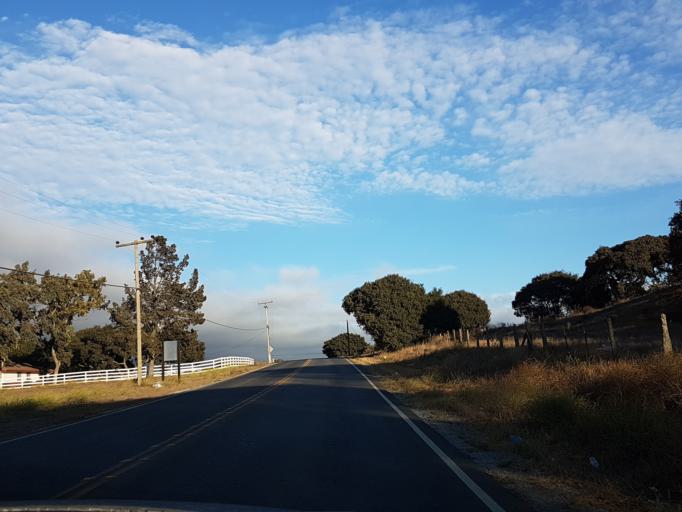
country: US
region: California
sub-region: Monterey County
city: Chualar
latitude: 36.5741
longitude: -121.5821
